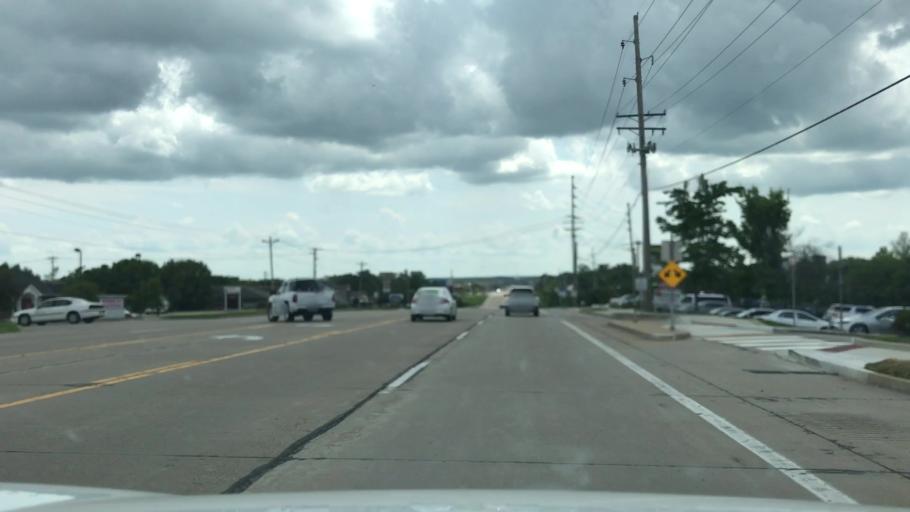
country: US
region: Missouri
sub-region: Saint Charles County
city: Dardenne Prairie
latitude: 38.7696
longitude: -90.7002
